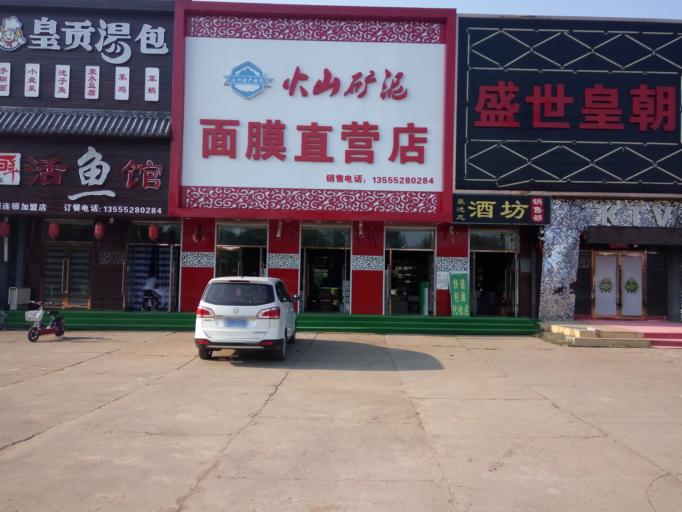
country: CN
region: Heilongjiang Sheng
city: Erjing
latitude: 48.6472
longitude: 126.1396
